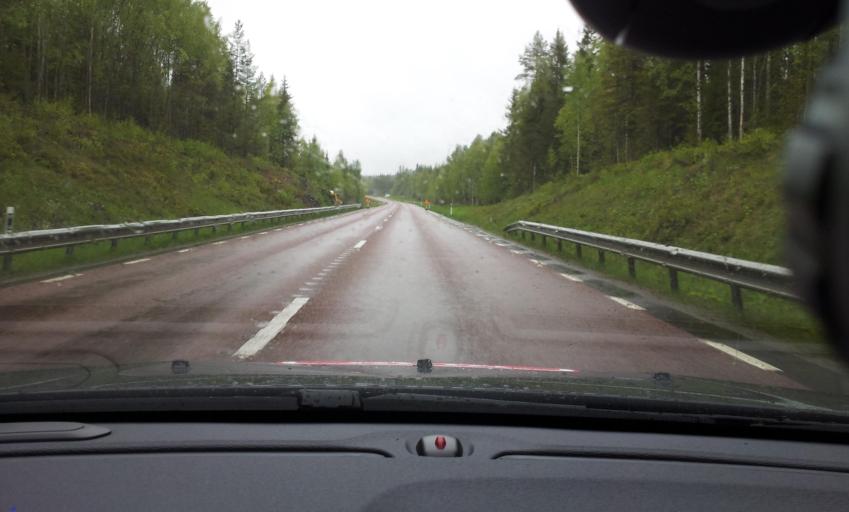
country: SE
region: Jaemtland
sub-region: Bergs Kommun
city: Hoverberg
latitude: 62.8861
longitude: 14.5234
